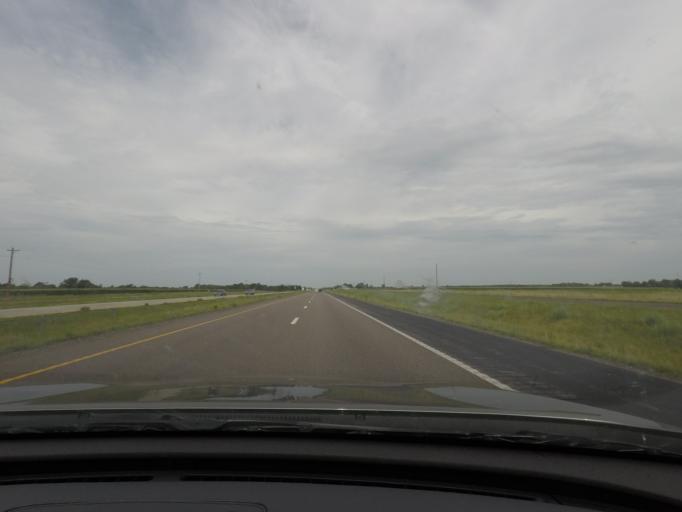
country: US
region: Missouri
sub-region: Callaway County
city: Fulton
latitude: 38.9197
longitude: -91.7530
